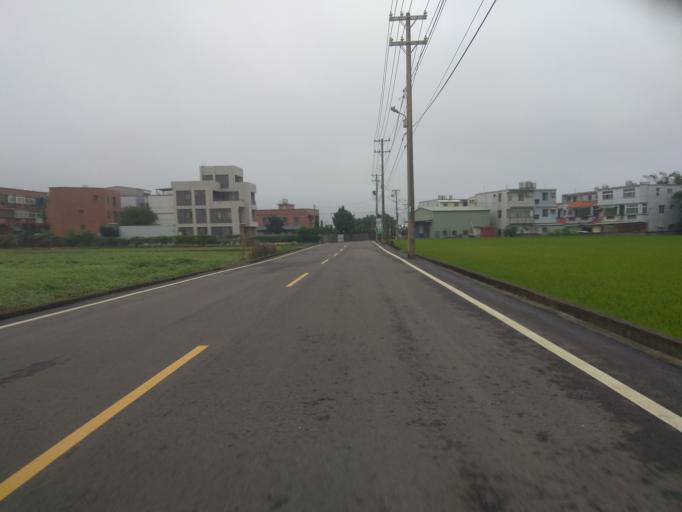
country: TW
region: Taiwan
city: Taoyuan City
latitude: 24.9959
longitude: 121.1244
